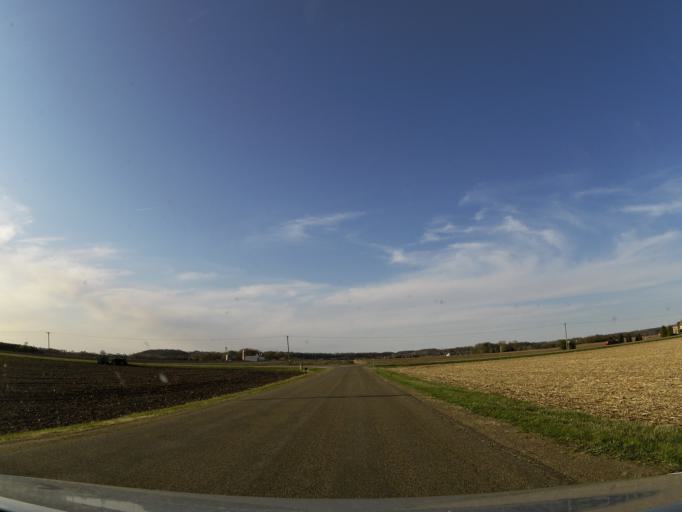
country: US
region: Minnesota
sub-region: Washington County
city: Lake Saint Croix Beach
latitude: 44.8612
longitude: -92.7160
